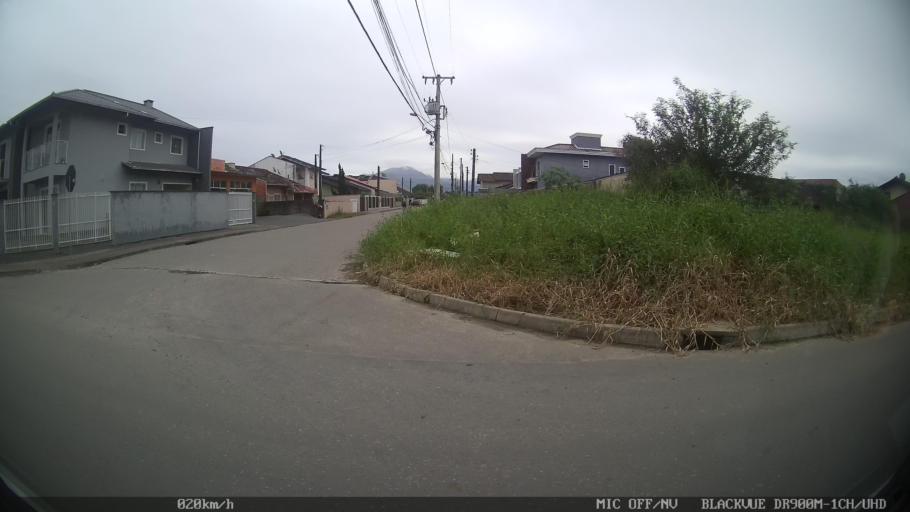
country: BR
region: Santa Catarina
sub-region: Joinville
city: Joinville
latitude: -26.2975
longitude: -48.9018
